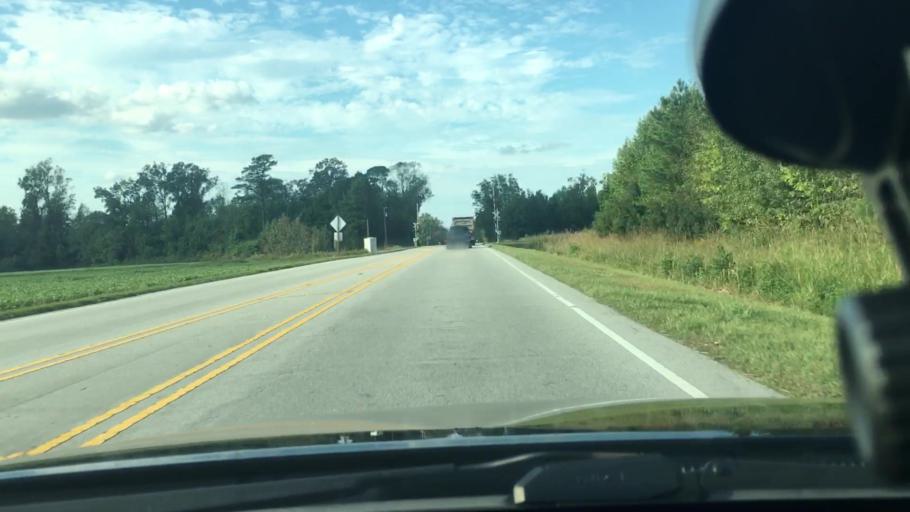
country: US
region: North Carolina
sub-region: Craven County
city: Vanceboro
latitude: 35.2909
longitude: -77.1294
